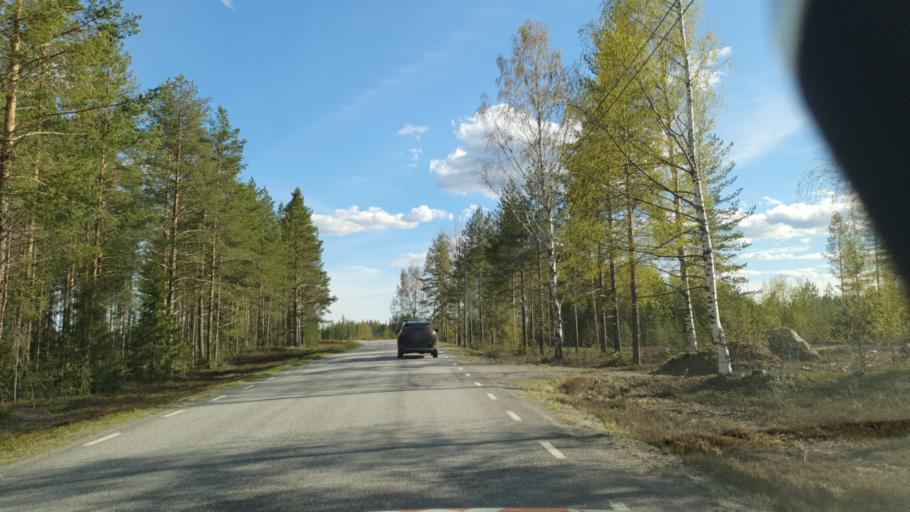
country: SE
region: Vaesterbotten
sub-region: Umea Kommun
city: Roback
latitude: 63.9172
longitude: 20.1445
